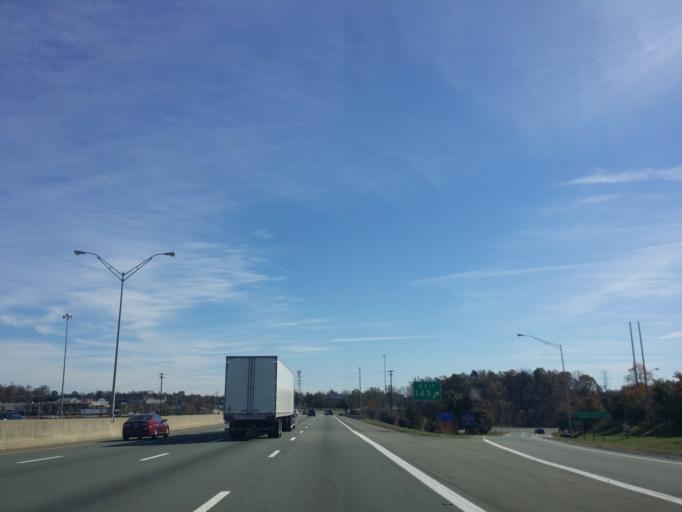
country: US
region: North Carolina
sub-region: Alamance County
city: Burlington
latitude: 36.0659
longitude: -79.4715
